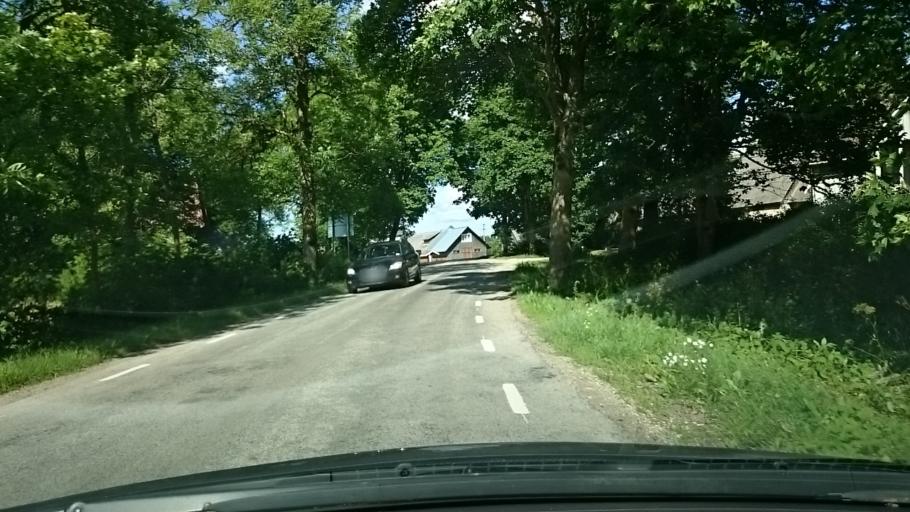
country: EE
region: Laeaene
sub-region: Haapsalu linn
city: Haapsalu
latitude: 59.0371
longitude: 23.5094
